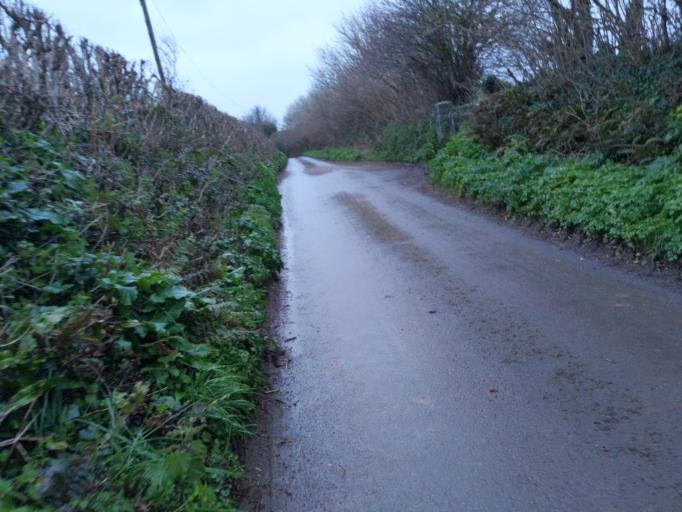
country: GB
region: England
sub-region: Devon
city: Yealmpton
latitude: 50.3245
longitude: -4.0295
